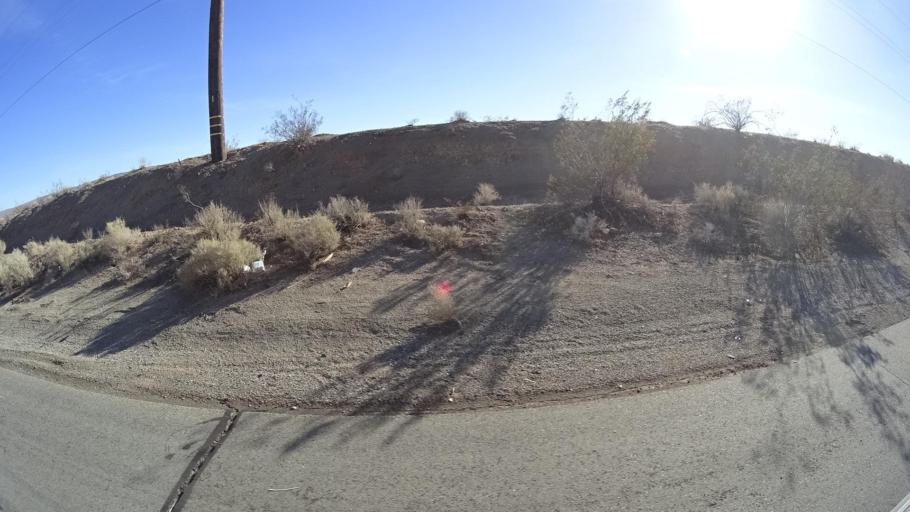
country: US
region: California
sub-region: Kern County
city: Ridgecrest
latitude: 35.6225
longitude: -117.7184
